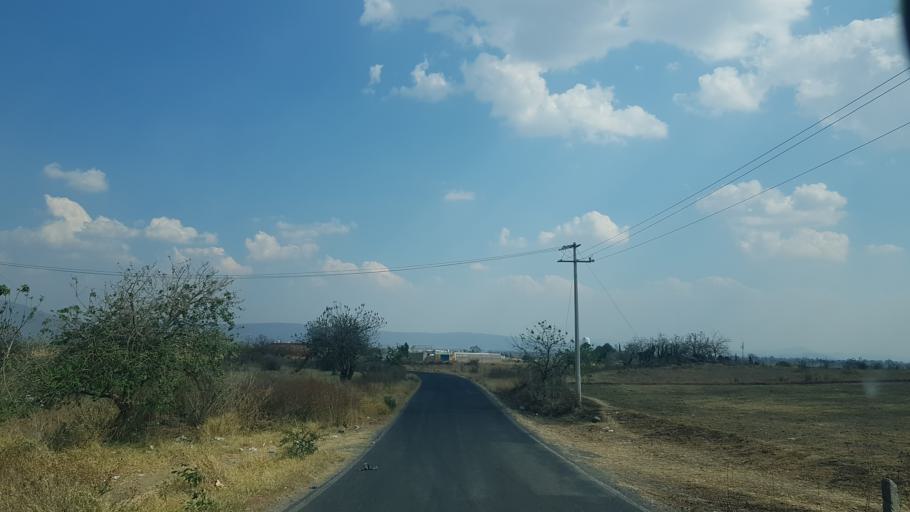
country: MX
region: Puebla
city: Atlixco
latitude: 18.9196
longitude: -98.4822
